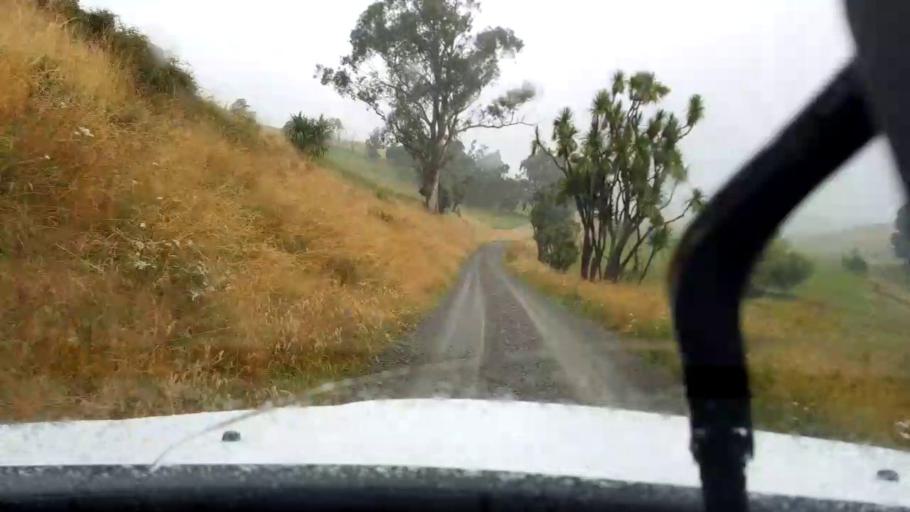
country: NZ
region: Canterbury
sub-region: Timaru District
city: Pleasant Point
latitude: -44.1897
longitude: 171.1031
